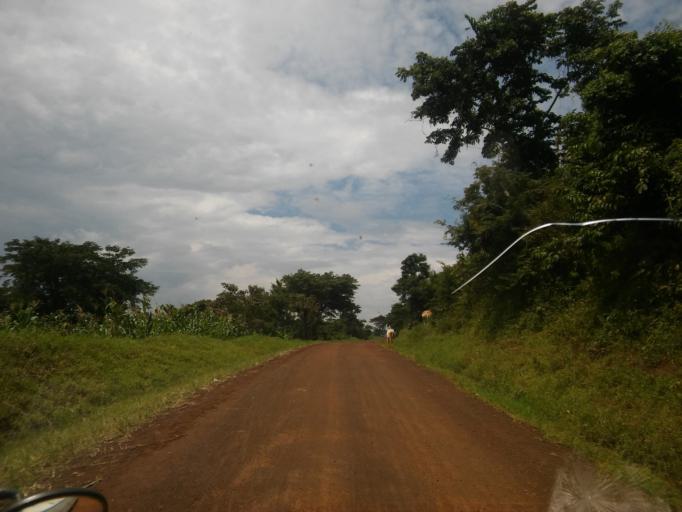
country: UG
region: Eastern Region
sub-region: Manafwa District
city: Manafwa
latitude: 0.8413
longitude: 34.2775
